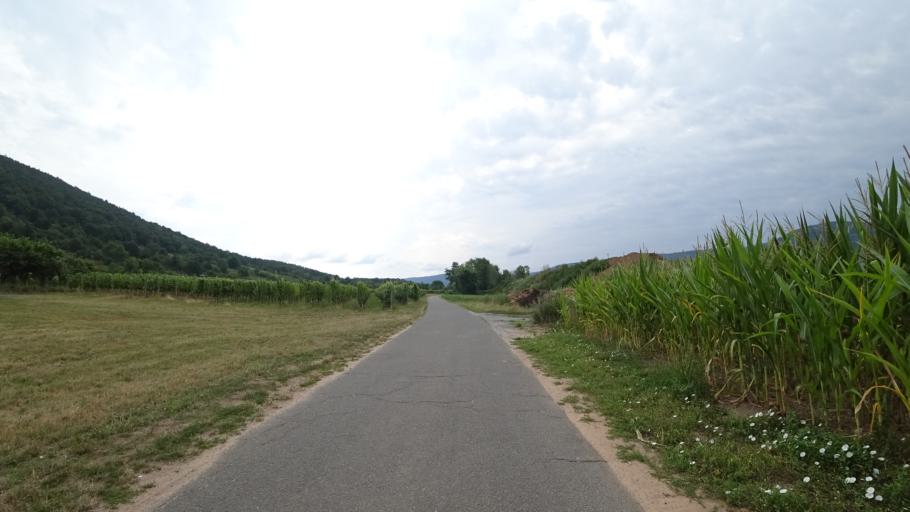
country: DE
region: Bavaria
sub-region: Regierungsbezirk Unterfranken
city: Grossheubach
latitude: 49.7195
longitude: 9.2394
